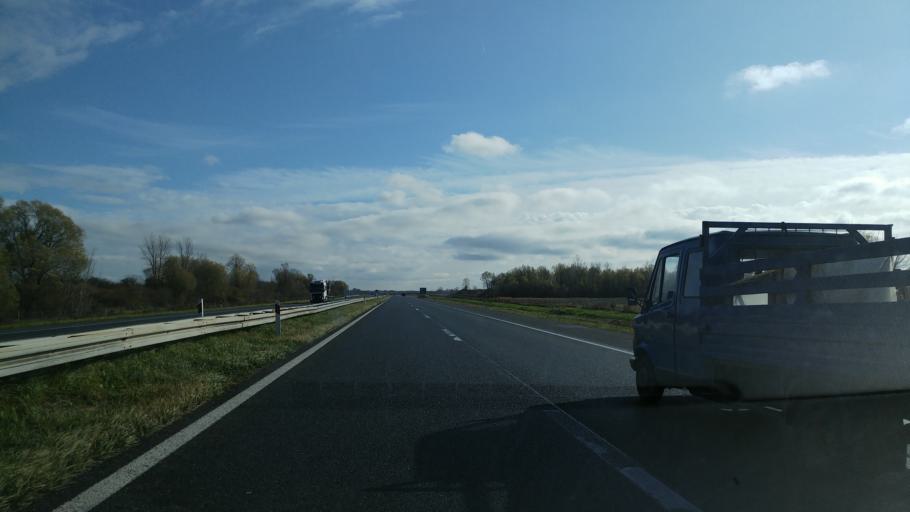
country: HR
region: Grad Zagreb
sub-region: Sesvete
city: Sesvete
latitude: 45.7779
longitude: 16.1965
